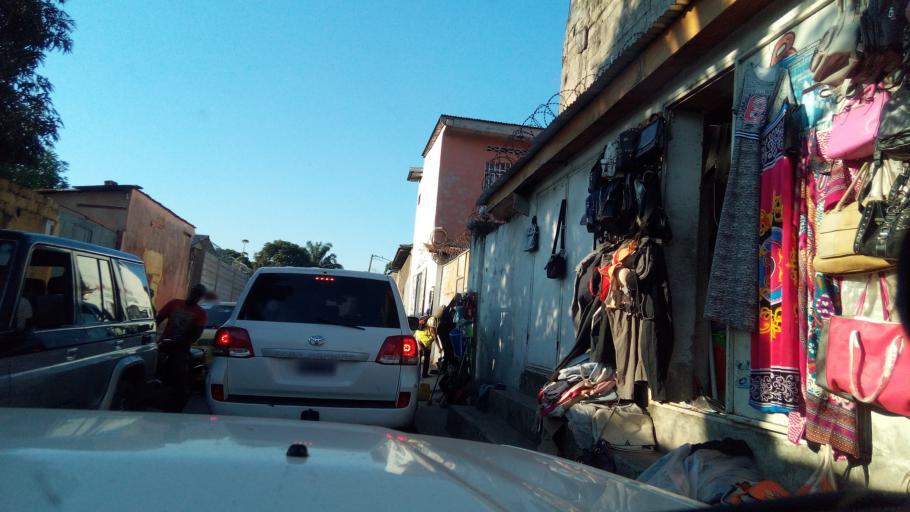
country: CD
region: Kinshasa
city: Kinshasa
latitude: -4.3450
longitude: 15.2689
